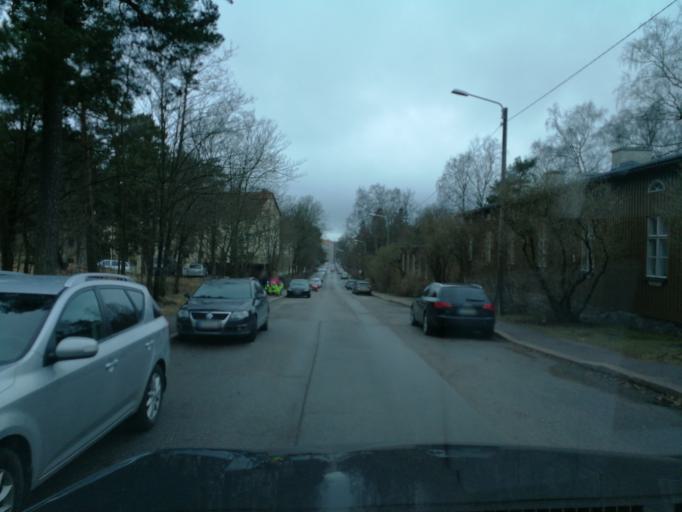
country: FI
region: Uusimaa
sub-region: Helsinki
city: Helsinki
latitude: 60.2129
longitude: 24.9518
